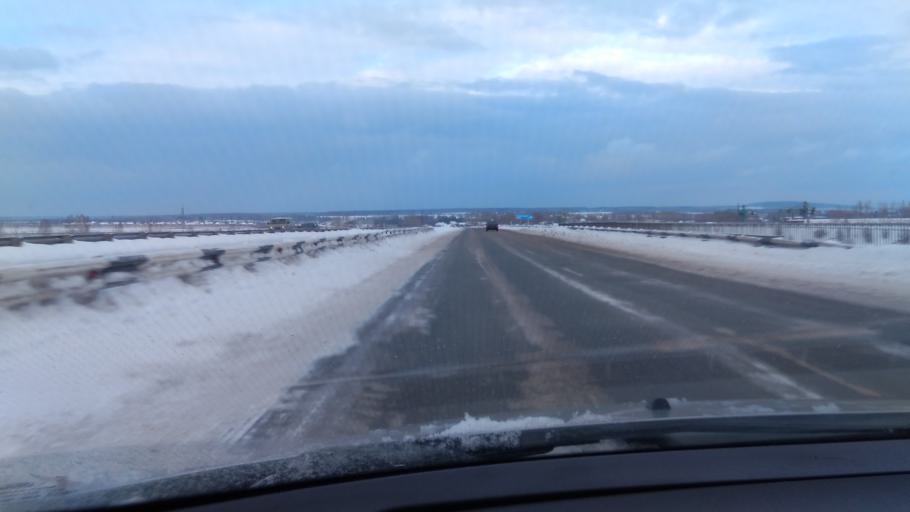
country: RU
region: Sverdlovsk
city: Tsementnyy
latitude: 57.4806
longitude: 60.1803
